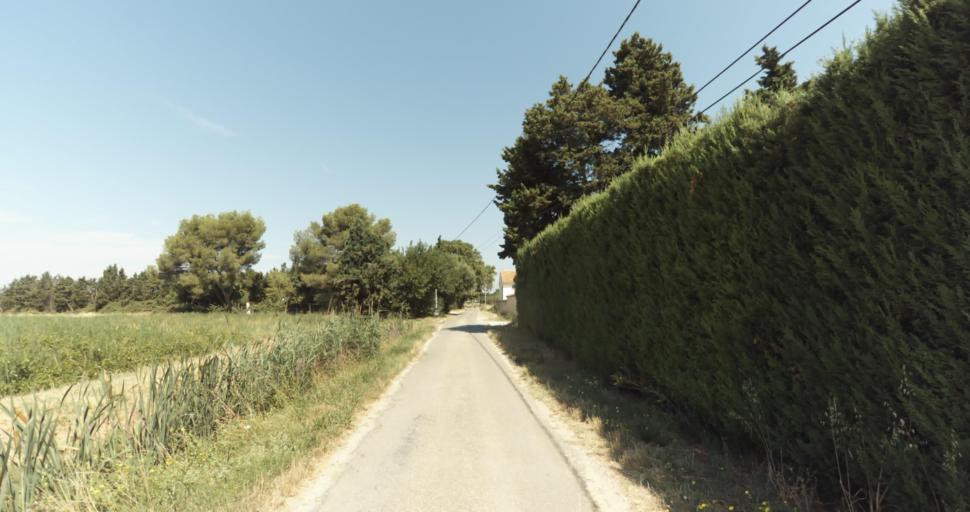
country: FR
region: Provence-Alpes-Cote d'Azur
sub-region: Departement du Vaucluse
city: Monteux
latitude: 44.0161
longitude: 5.0157
